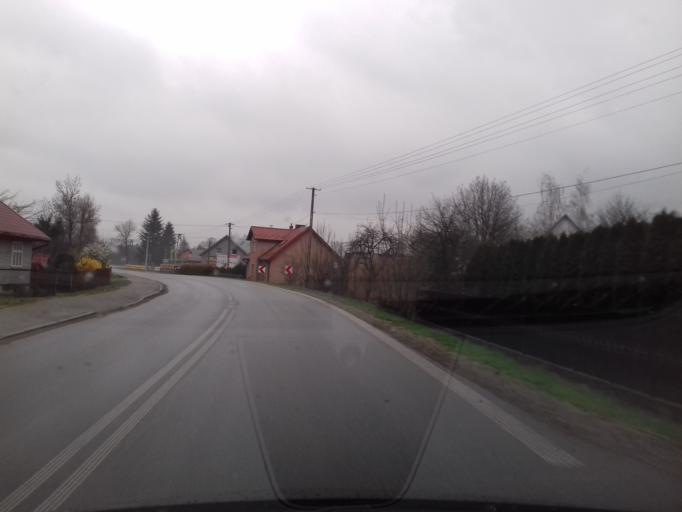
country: PL
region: Lesser Poland Voivodeship
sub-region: Powiat nowosadecki
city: Stary Sacz
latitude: 49.5969
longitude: 20.6358
